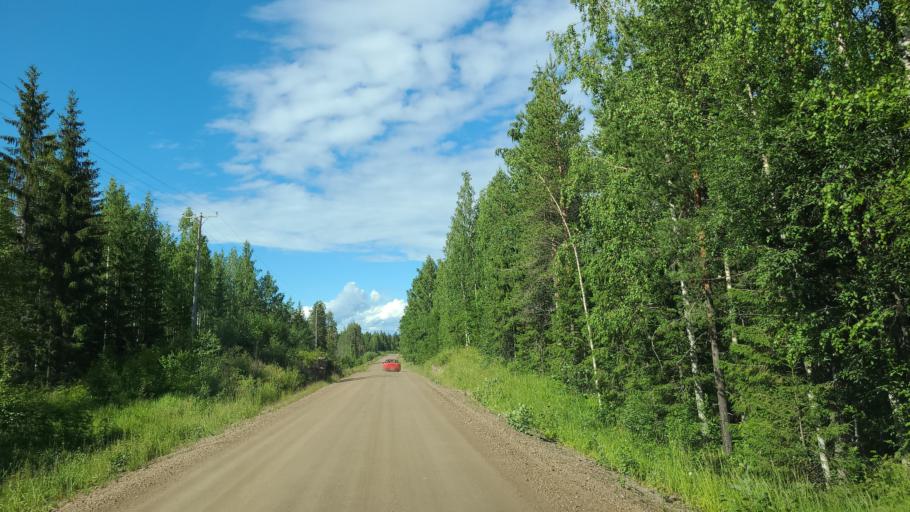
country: FI
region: Northern Savo
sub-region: Koillis-Savo
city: Kaavi
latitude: 62.9384
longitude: 28.7633
